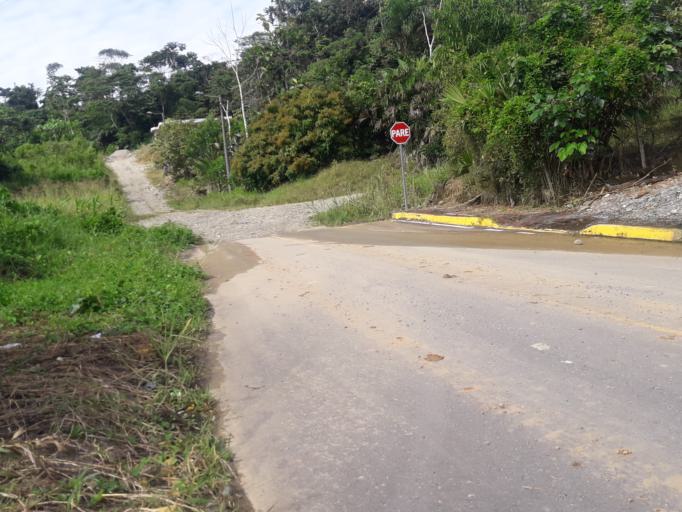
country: EC
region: Napo
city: Tena
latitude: -1.0103
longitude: -77.8140
